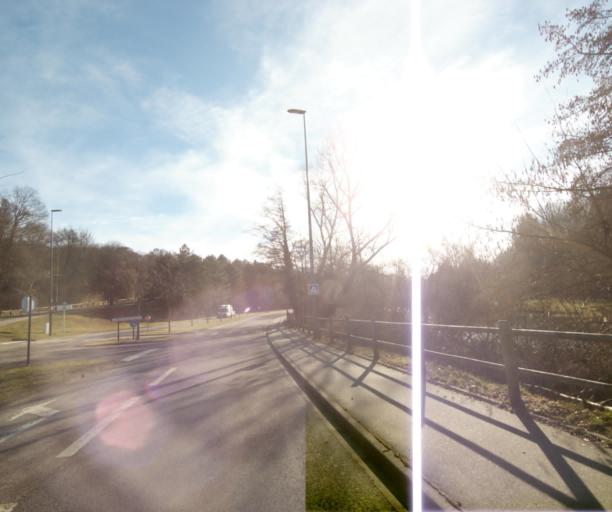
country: FR
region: Lorraine
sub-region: Departement de Meurthe-et-Moselle
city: Chavigny
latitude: 48.6586
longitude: 6.1174
